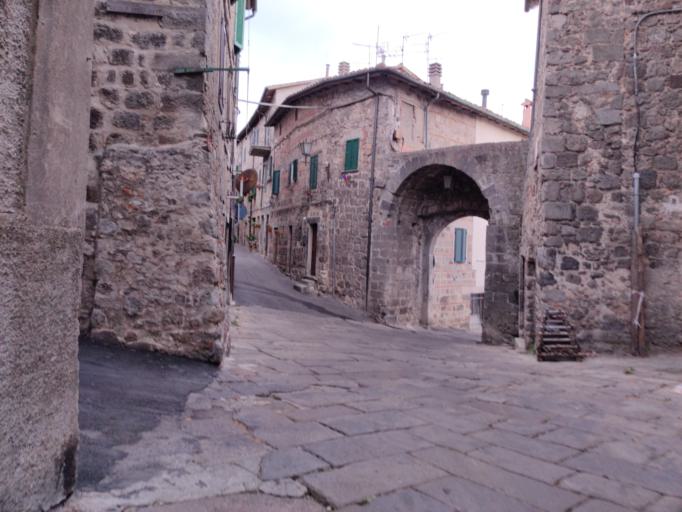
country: IT
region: Tuscany
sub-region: Provincia di Siena
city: Abbadia San Salvatore
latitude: 42.8787
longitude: 11.6788
